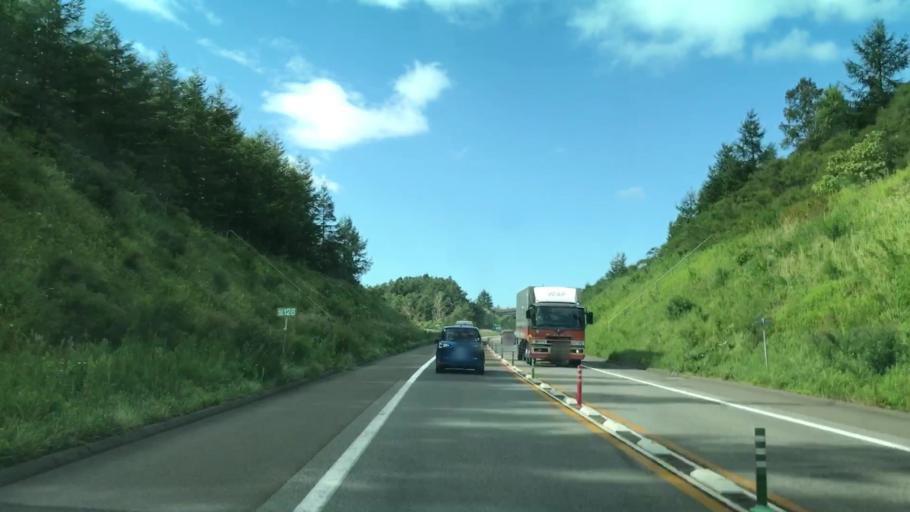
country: JP
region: Hokkaido
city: Date
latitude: 42.4424
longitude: 140.9163
